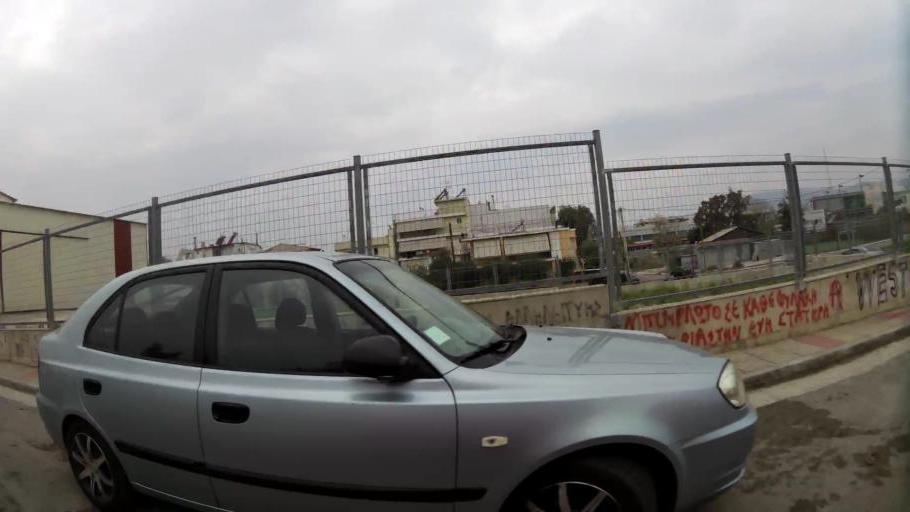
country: GR
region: Attica
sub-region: Nomarchia Athinas
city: Agioi Anargyroi
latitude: 38.0371
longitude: 23.7150
